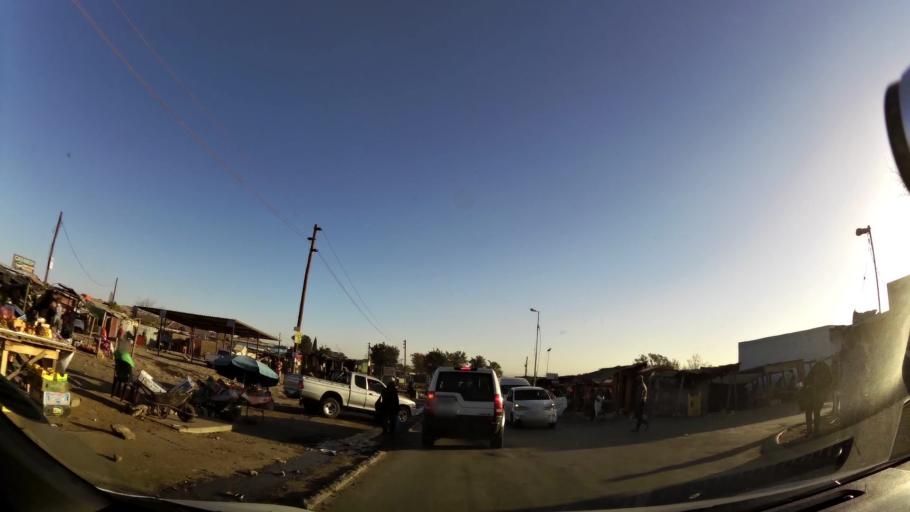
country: ZA
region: Gauteng
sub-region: City of Johannesburg Metropolitan Municipality
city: Diepsloot
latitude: -25.9316
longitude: 28.0158
